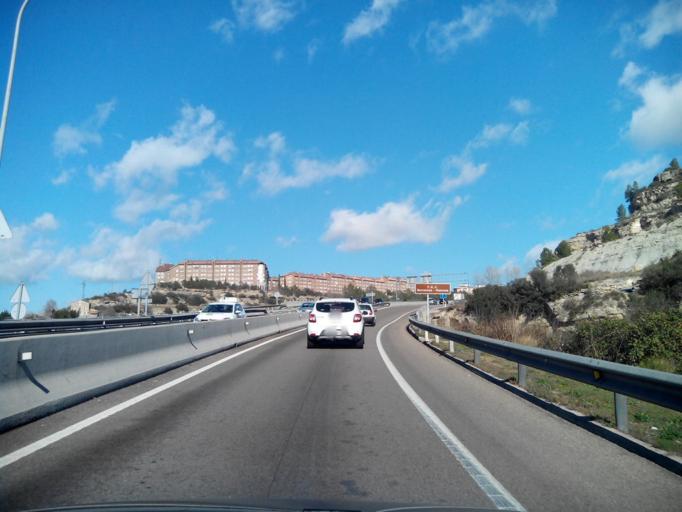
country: ES
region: Catalonia
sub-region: Provincia de Barcelona
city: Manresa
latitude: 41.7123
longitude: 1.8354
